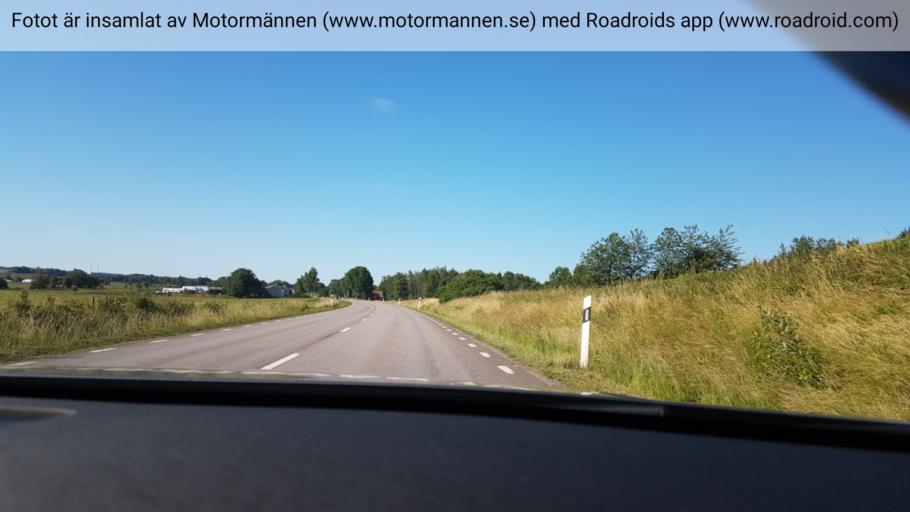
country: SE
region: Vaestra Goetaland
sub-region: Falkopings Kommun
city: Falkoeping
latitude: 58.1005
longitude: 13.5302
